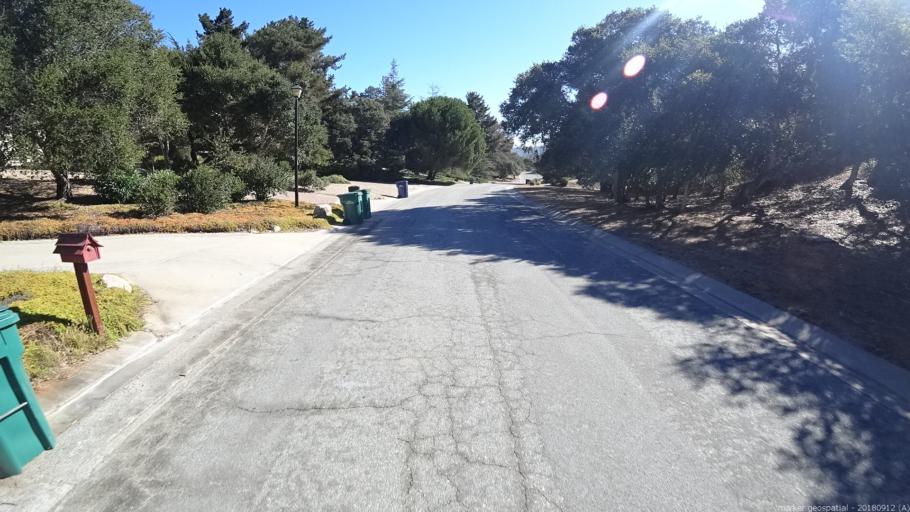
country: US
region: California
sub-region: Monterey County
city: Carmel Valley Village
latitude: 36.5656
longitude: -121.7414
